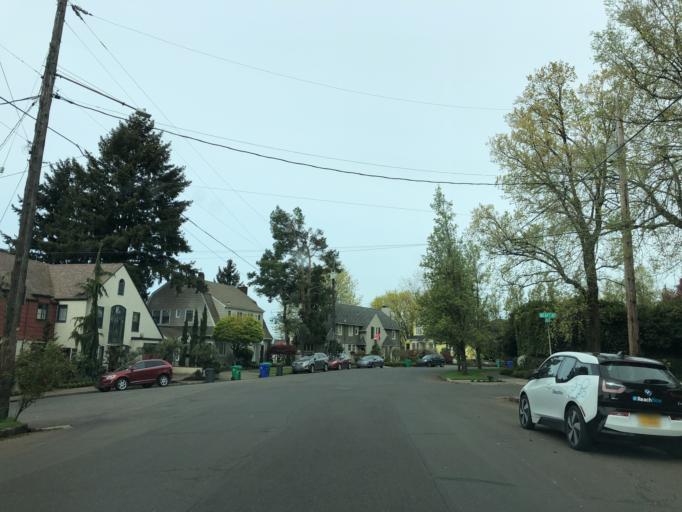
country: US
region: Oregon
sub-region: Multnomah County
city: Portland
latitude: 45.5509
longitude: -122.6400
